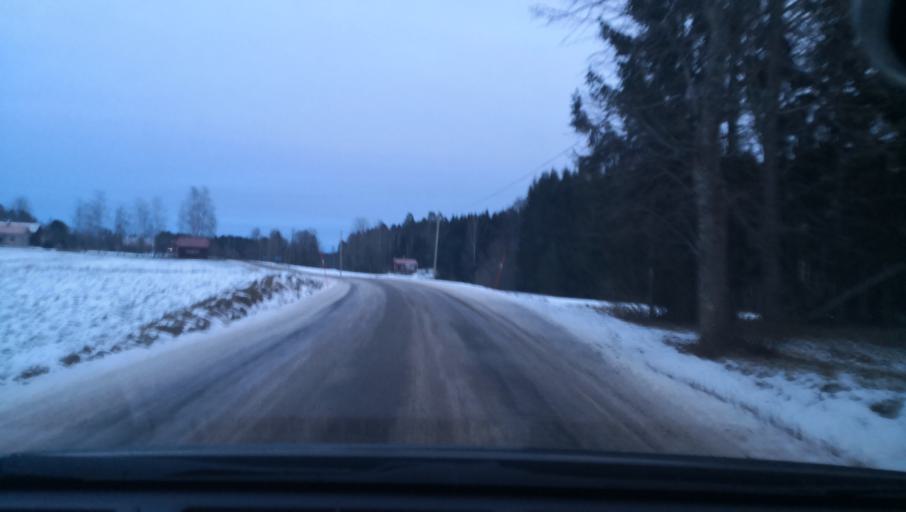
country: SE
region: Dalarna
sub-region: Avesta Kommun
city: Horndal
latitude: 60.2006
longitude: 16.5075
